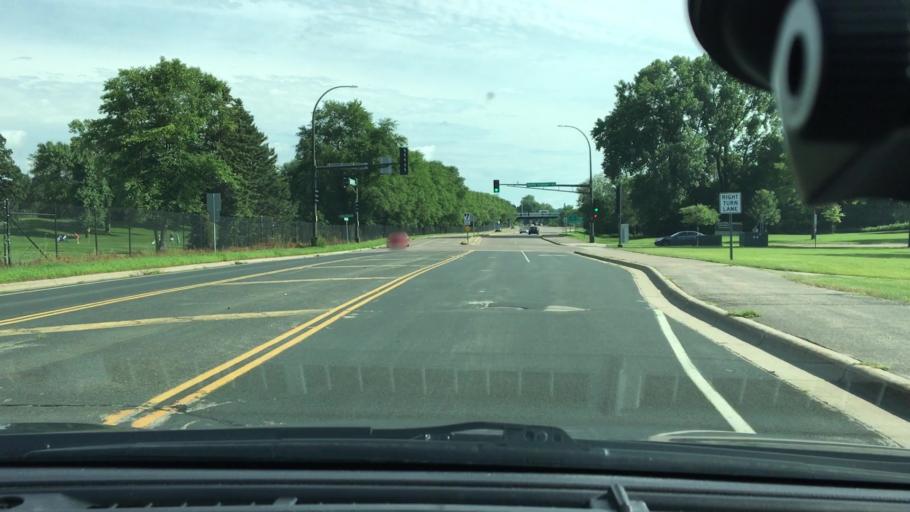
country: US
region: Minnesota
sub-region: Hennepin County
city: Golden Valley
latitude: 44.9794
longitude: -93.3905
